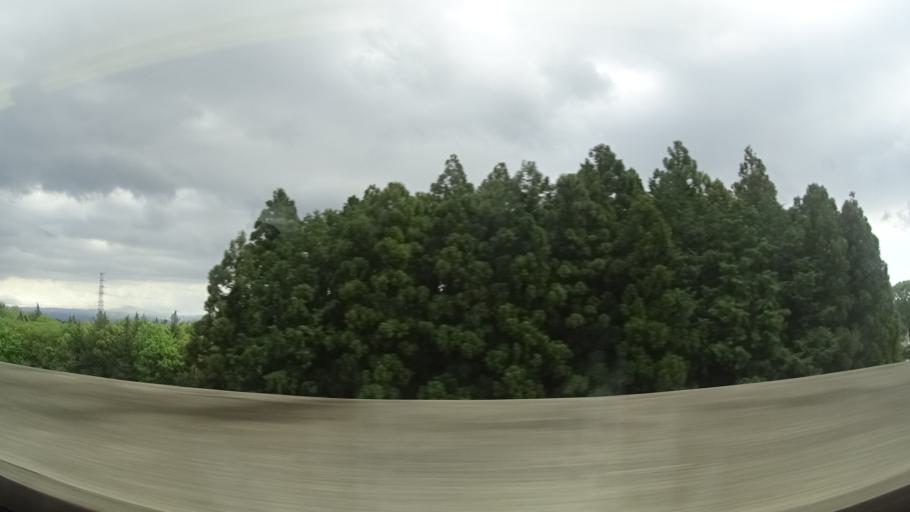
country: JP
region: Tochigi
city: Kuroiso
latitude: 36.9433
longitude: 140.0332
